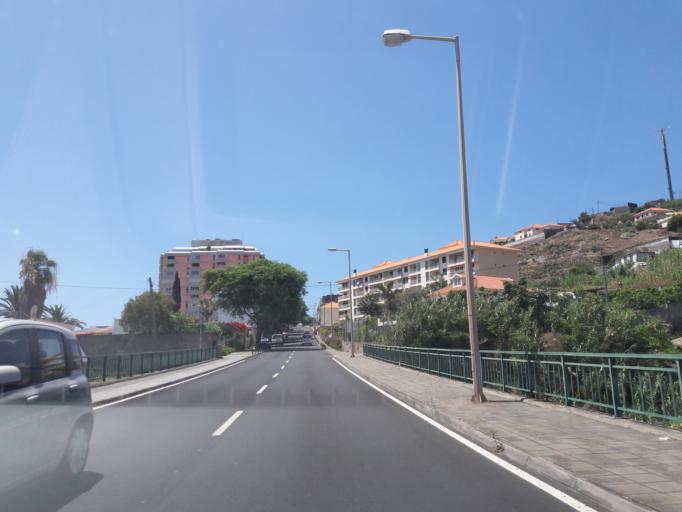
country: PT
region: Madeira
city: Canico
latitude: 32.6457
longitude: -16.8285
